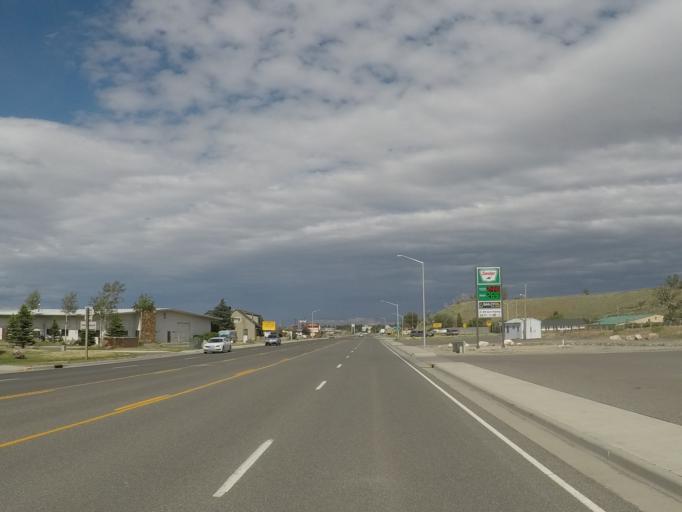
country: US
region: Wyoming
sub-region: Park County
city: Cody
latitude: 44.5147
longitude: -109.0988
